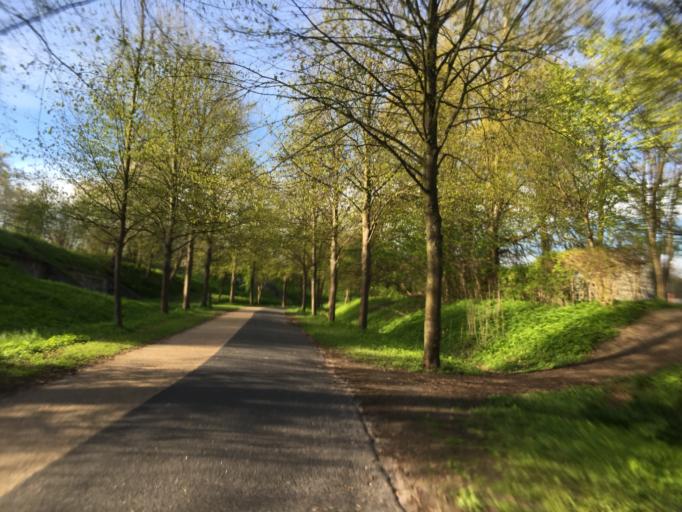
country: DK
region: Capital Region
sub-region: Herlev Kommune
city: Herlev
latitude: 55.7117
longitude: 12.4633
